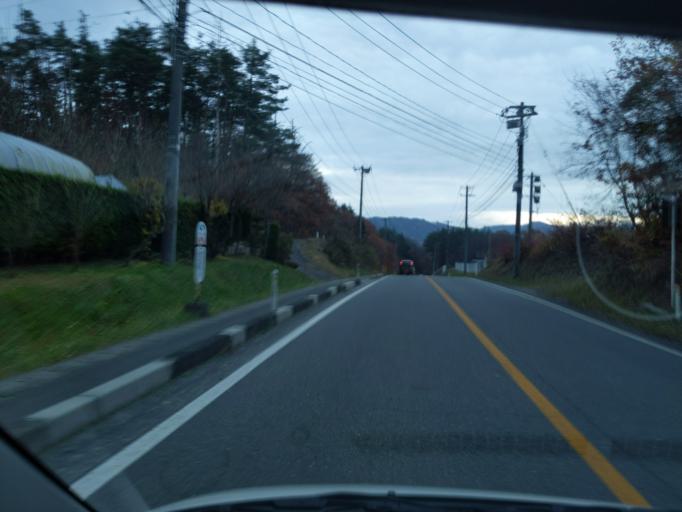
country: JP
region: Iwate
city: Ichinoseki
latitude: 39.0042
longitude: 141.3260
